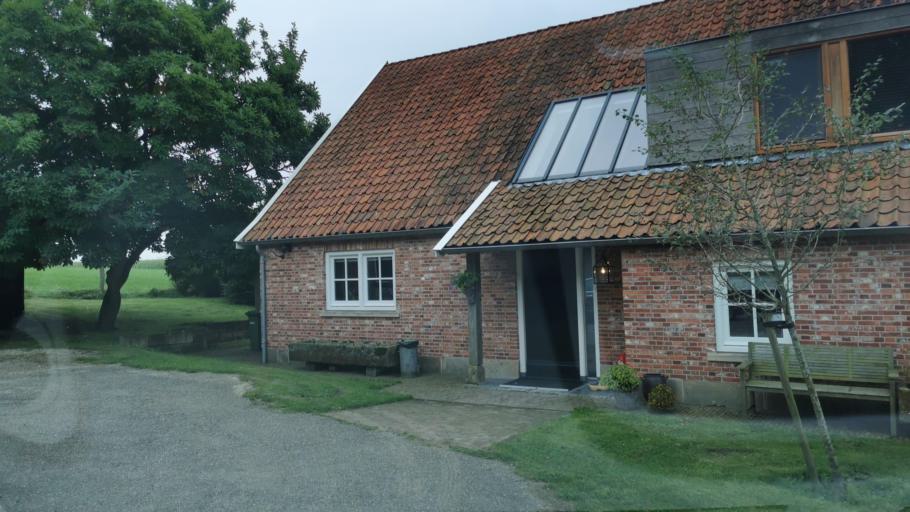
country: NL
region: Overijssel
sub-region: Gemeente Oldenzaal
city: Oldenzaal
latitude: 52.3145
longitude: 6.9625
